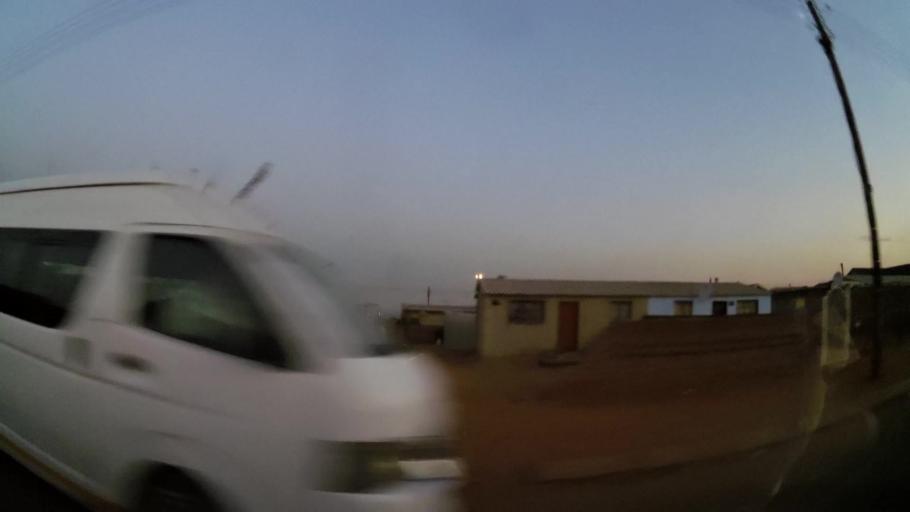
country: ZA
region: Gauteng
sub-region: West Rand District Municipality
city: Randfontein
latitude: -26.2086
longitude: 27.7087
